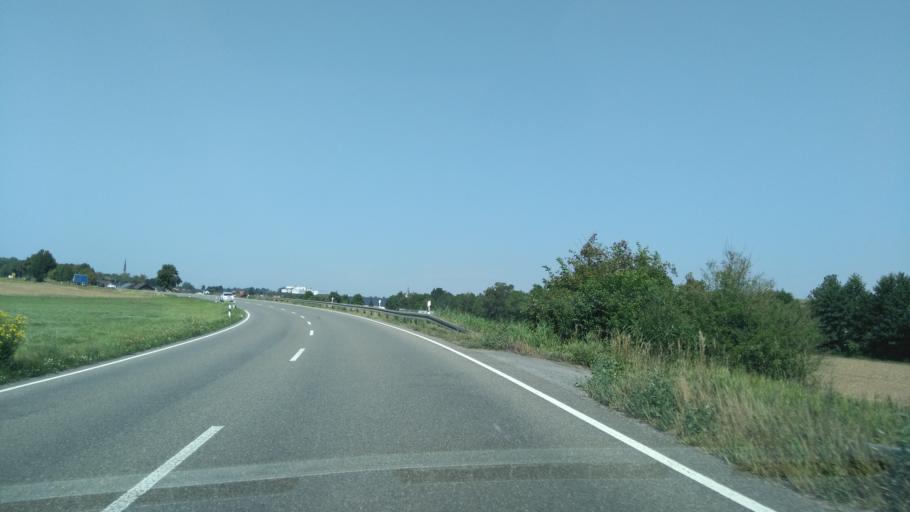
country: DE
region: Baden-Wuerttemberg
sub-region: Karlsruhe Region
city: Muhlacker
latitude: 48.9699
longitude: 8.8732
